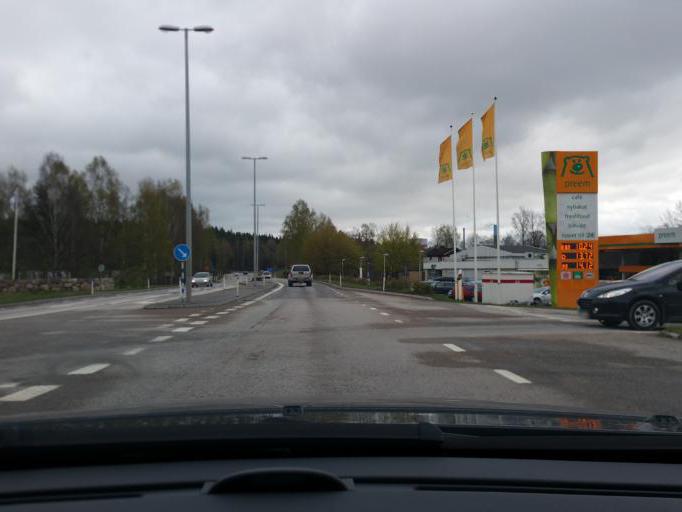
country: SE
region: Kronoberg
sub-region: Vaxjo Kommun
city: Vaexjoe
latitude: 56.8794
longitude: 14.8332
